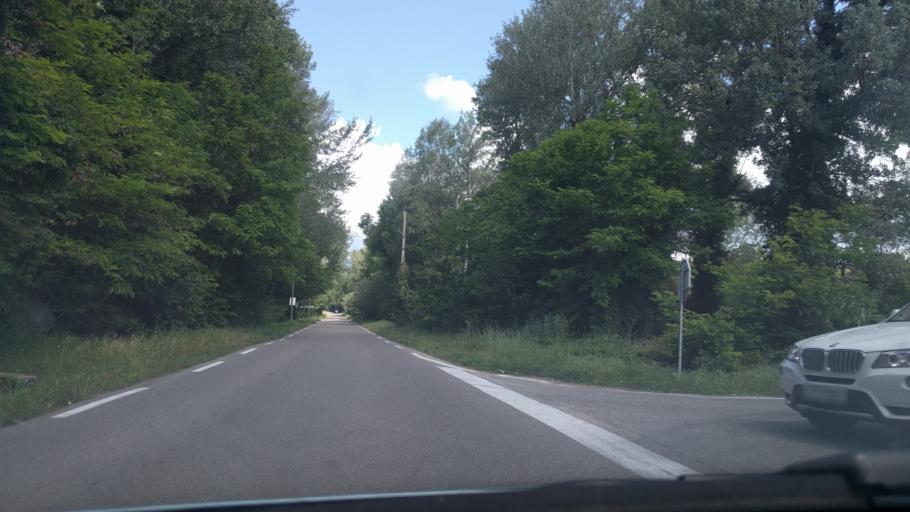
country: FR
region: Provence-Alpes-Cote d'Azur
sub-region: Departement du Vaucluse
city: Pertuis
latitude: 43.7466
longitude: 5.5247
